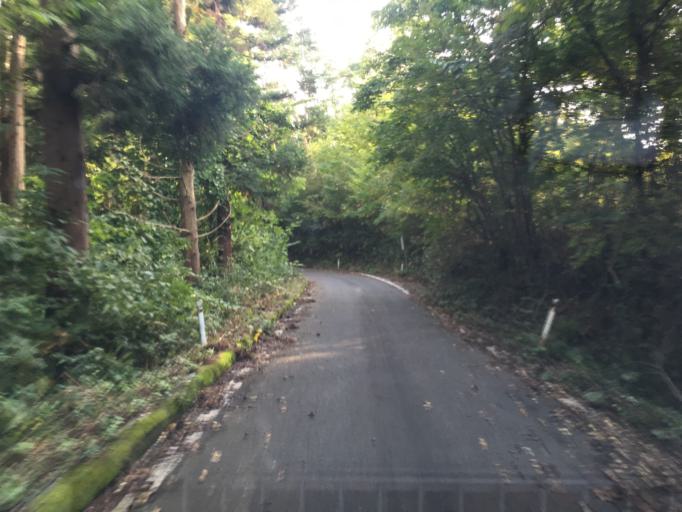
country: JP
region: Fukushima
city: Yanagawamachi-saiwaicho
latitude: 37.8954
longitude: 140.5436
